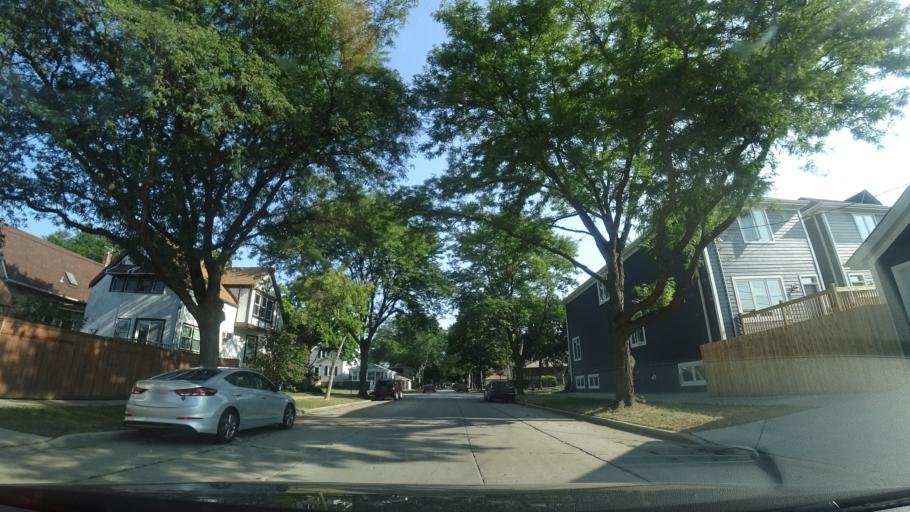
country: US
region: Illinois
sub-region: Cook County
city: Harwood Heights
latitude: 41.9650
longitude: -87.7649
